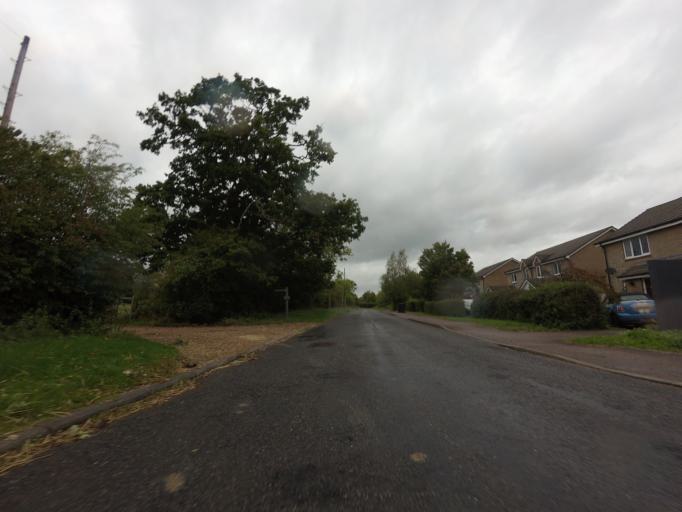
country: GB
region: England
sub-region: Cambridgeshire
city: Comberton
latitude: 52.1639
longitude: -0.0097
